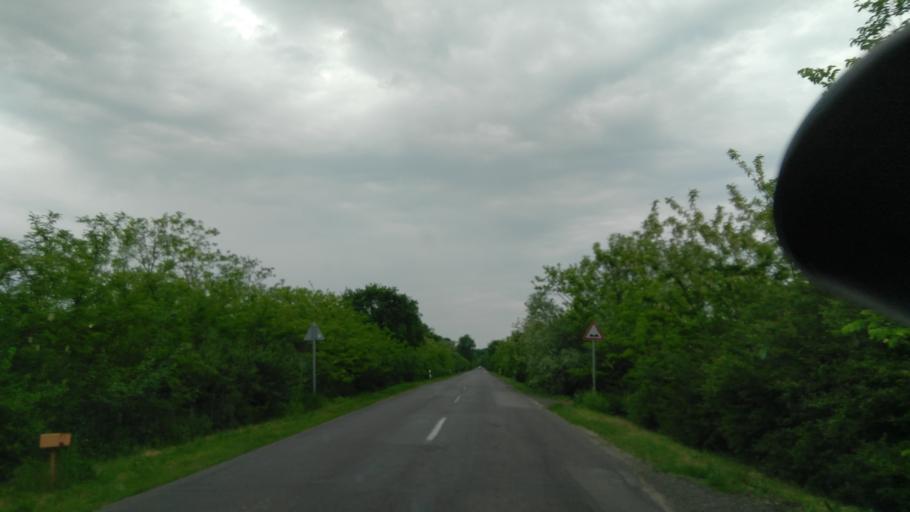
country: HU
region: Bekes
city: Doboz
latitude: 46.7222
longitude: 21.3070
